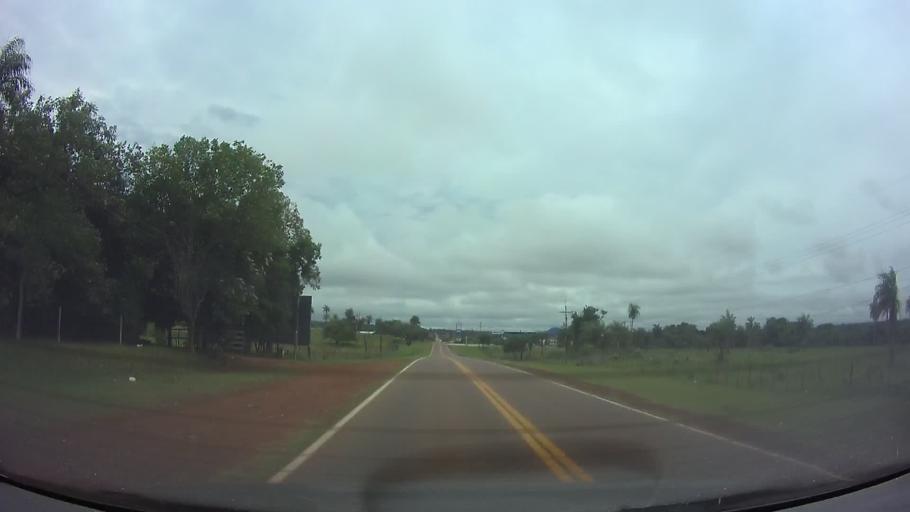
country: PY
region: Paraguari
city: Acahay
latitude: -25.9020
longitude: -57.1164
